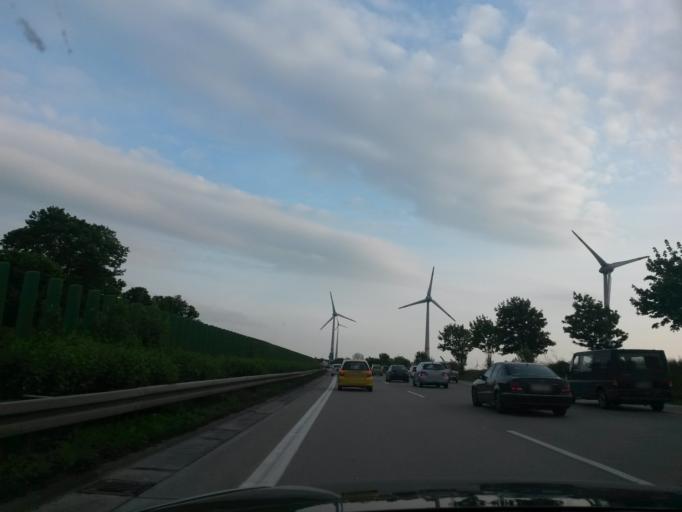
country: DE
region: Saxony-Anhalt
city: Stossen
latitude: 51.1254
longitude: 11.9591
